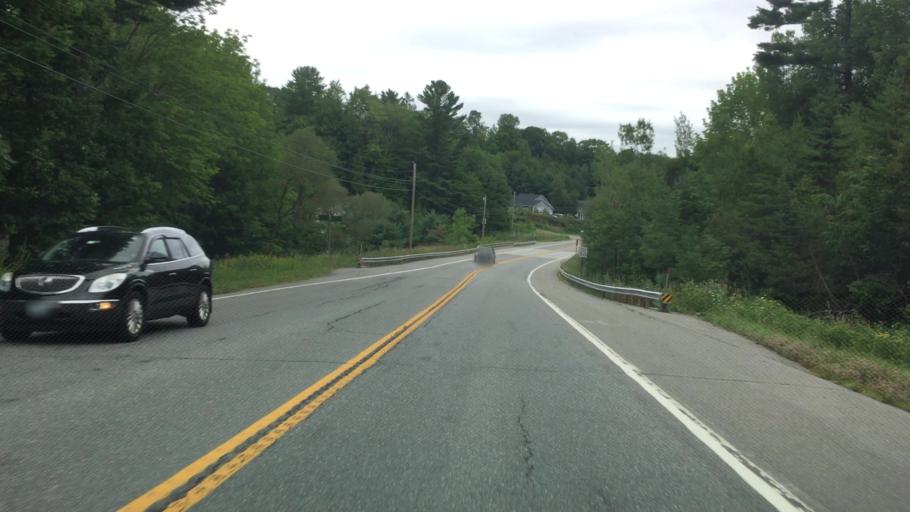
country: US
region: Maine
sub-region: Penobscot County
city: Orrington
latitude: 44.6932
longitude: -68.8478
